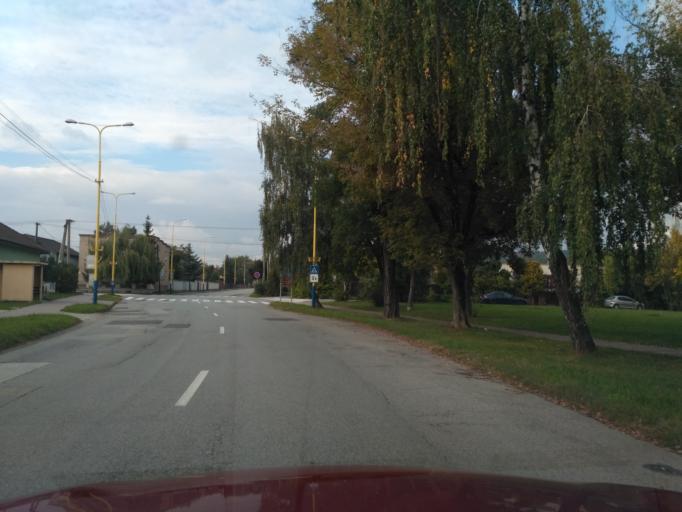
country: SK
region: Kosicky
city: Kosice
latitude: 48.6364
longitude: 21.1719
